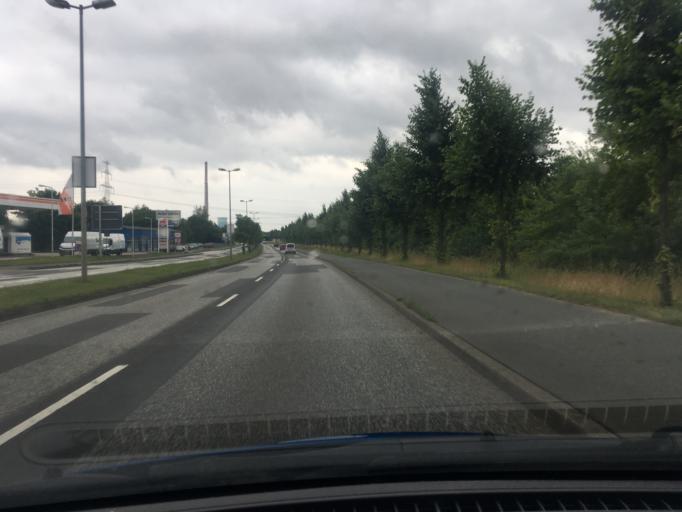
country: DE
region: Mecklenburg-Vorpommern
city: Feldstadt
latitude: 53.5899
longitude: 11.4028
